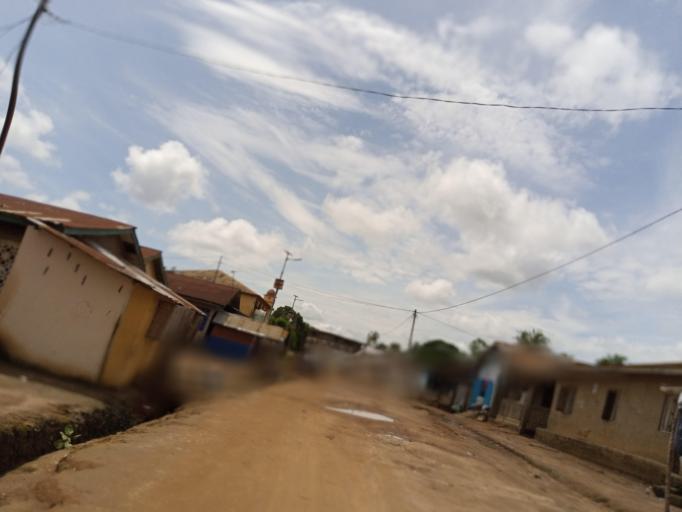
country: SL
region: Northern Province
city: Masoyila
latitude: 8.6108
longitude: -13.1895
